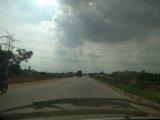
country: IN
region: Karnataka
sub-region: Bangalore Rural
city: Dasarahalli
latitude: 13.1326
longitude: 77.9511
